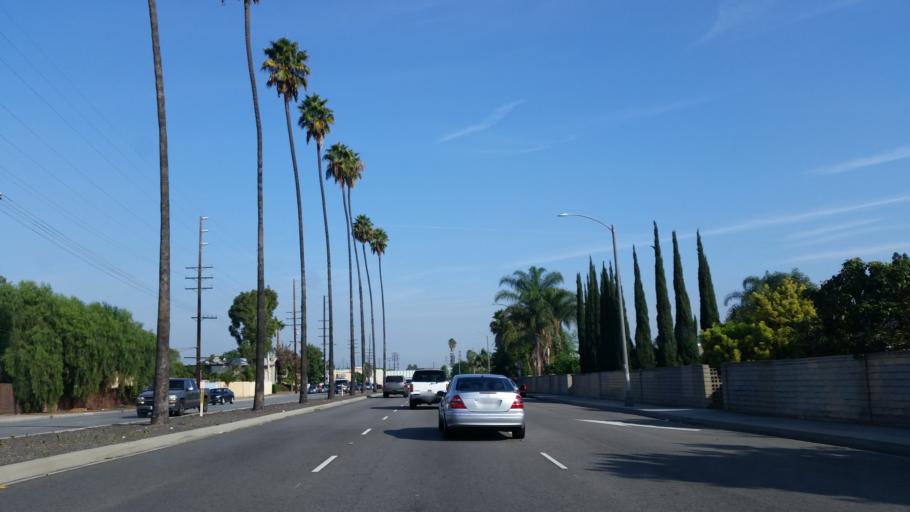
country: US
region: California
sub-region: Los Angeles County
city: Lakewood
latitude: 33.8492
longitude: -118.1675
